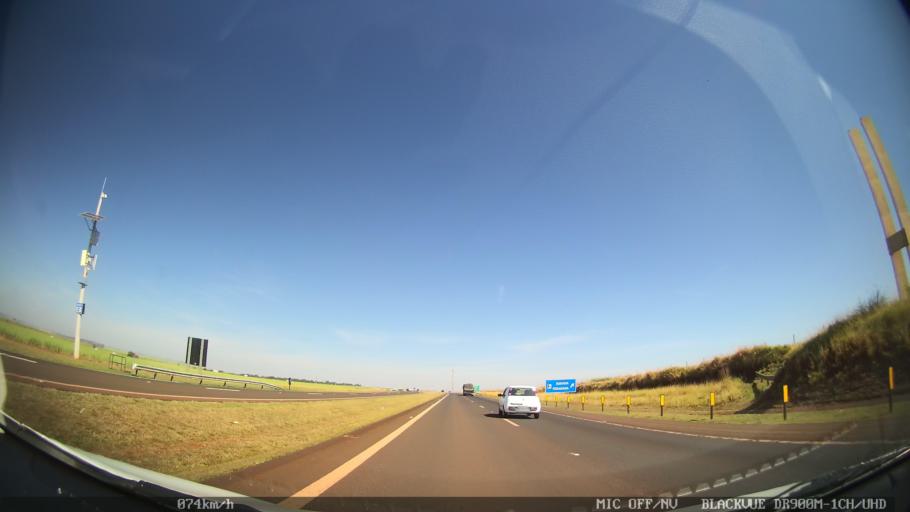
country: BR
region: Sao Paulo
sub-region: Ribeirao Preto
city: Ribeirao Preto
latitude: -21.1613
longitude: -47.8971
